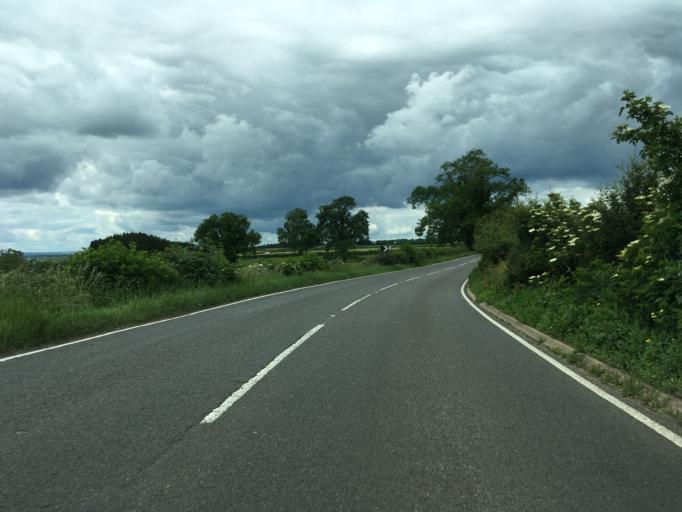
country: GB
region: England
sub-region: Northamptonshire
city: Brackley
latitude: 52.0892
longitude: -1.2092
